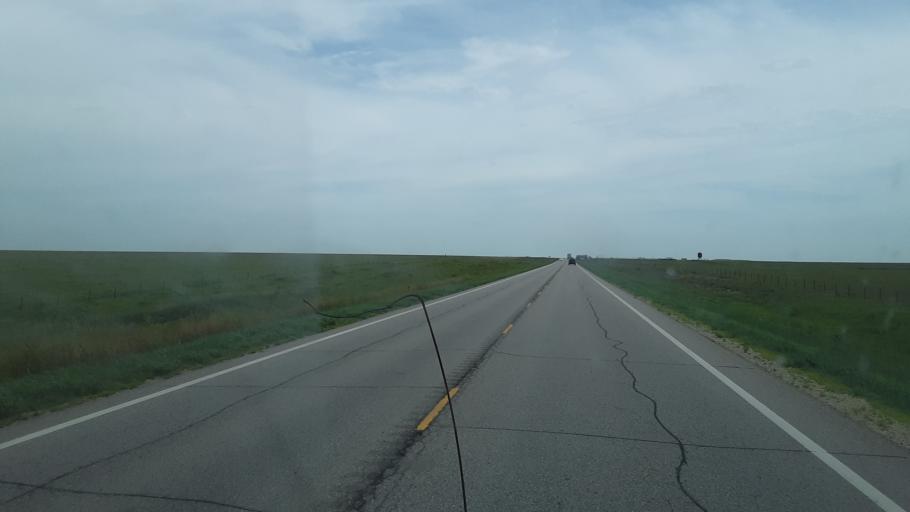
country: US
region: Kansas
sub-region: Greenwood County
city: Eureka
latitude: 37.8101
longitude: -96.5700
